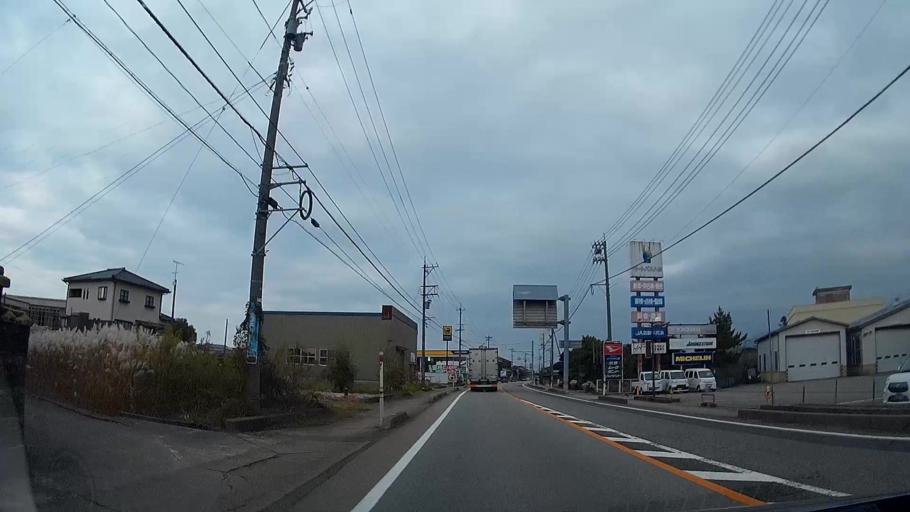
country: JP
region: Toyama
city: Nyuzen
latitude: 36.9353
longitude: 137.5057
